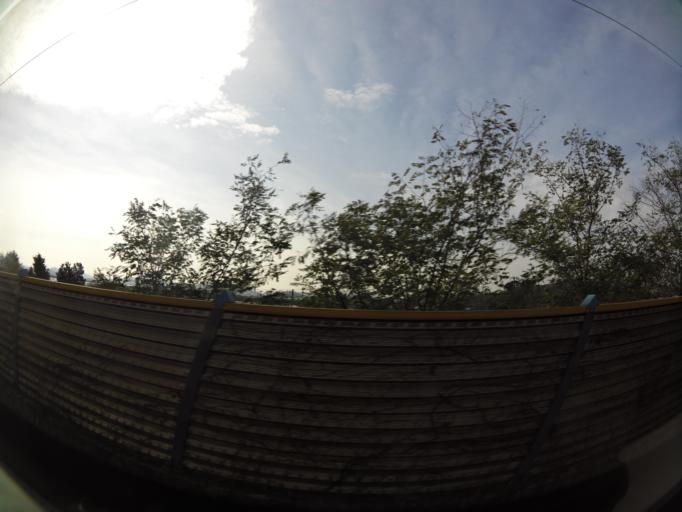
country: KR
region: Daejeon
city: Songgang-dong
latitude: 36.5766
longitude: 127.3111
